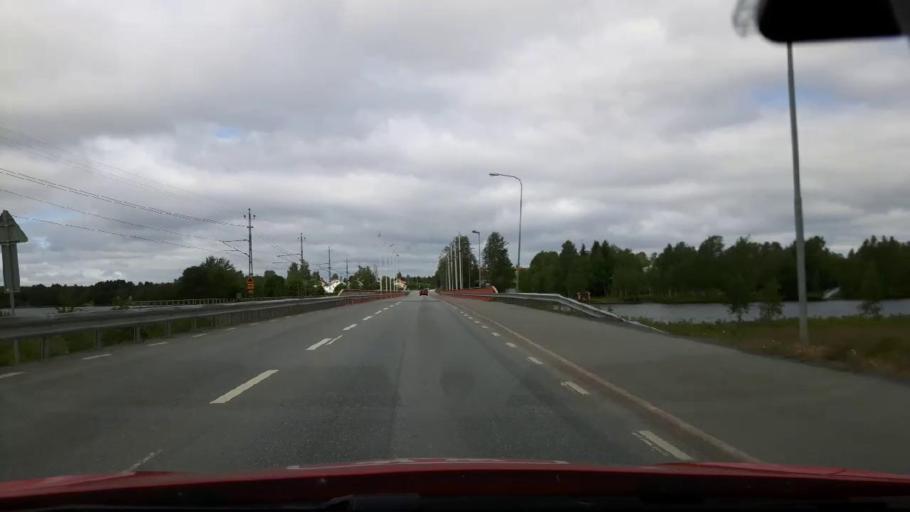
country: SE
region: Jaemtland
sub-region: Krokoms Kommun
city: Krokom
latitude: 63.3221
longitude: 14.4545
